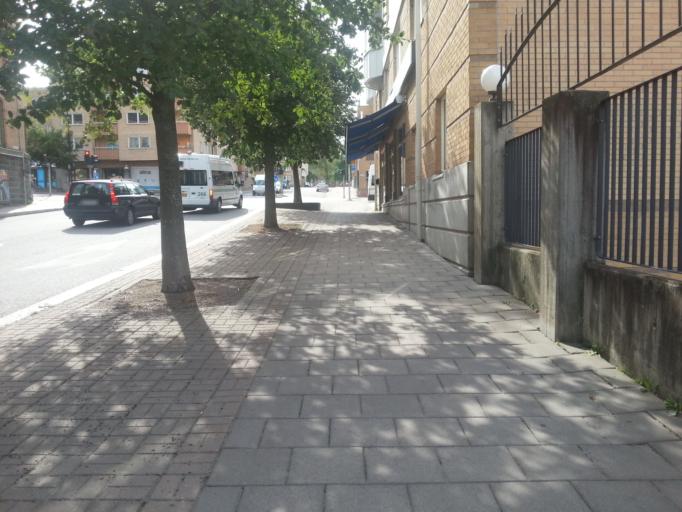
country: SE
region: OEstergoetland
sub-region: Norrkopings Kommun
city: Norrkoping
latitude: 58.5940
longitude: 16.1778
